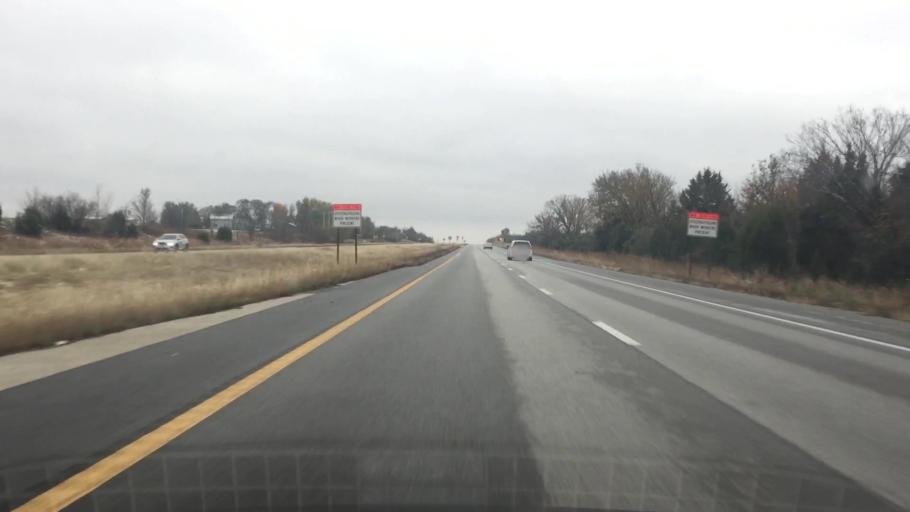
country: US
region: Missouri
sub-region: Henry County
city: Clinton
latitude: 38.3045
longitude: -93.7587
